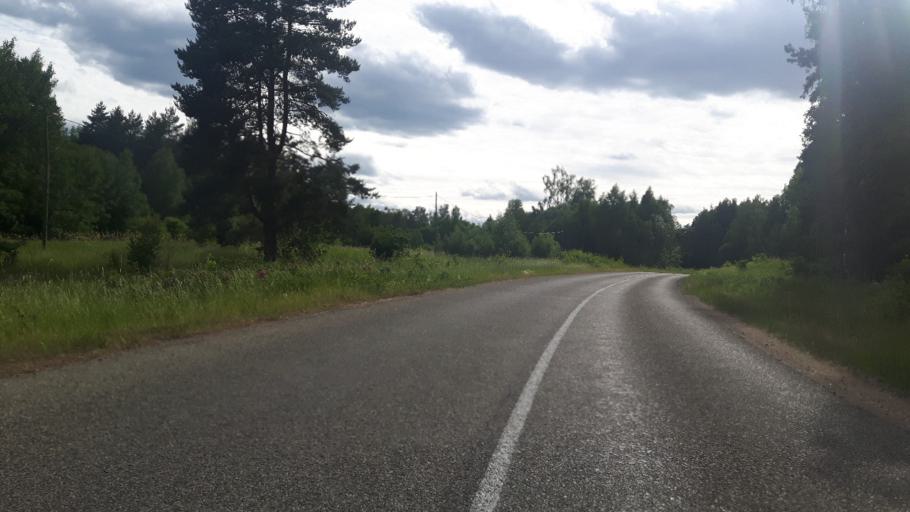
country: LV
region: Engure
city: Smarde
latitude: 56.9909
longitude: 23.3067
